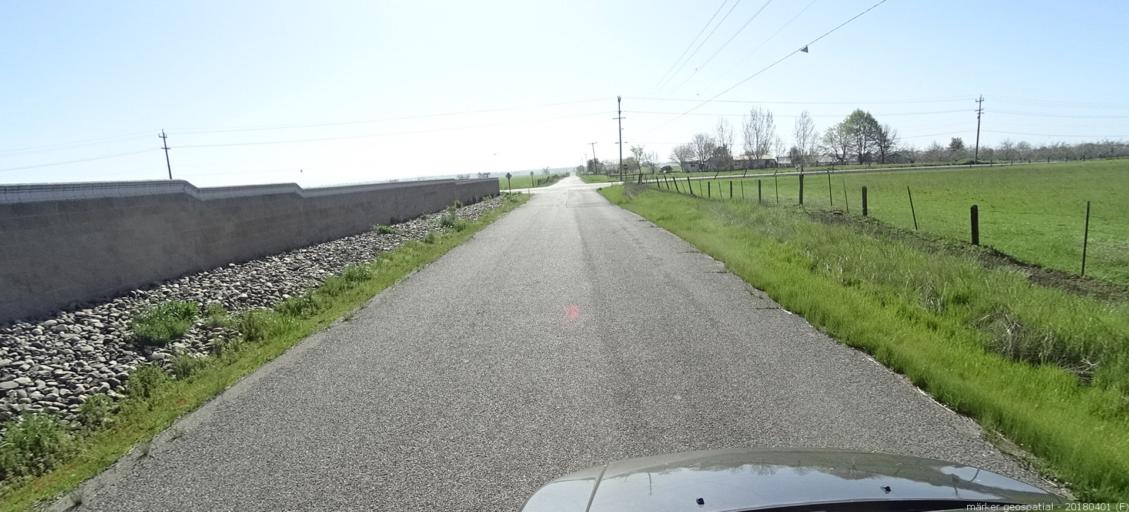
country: US
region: California
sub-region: Sacramento County
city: Rancho Murieta
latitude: 38.4748
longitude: -121.1720
